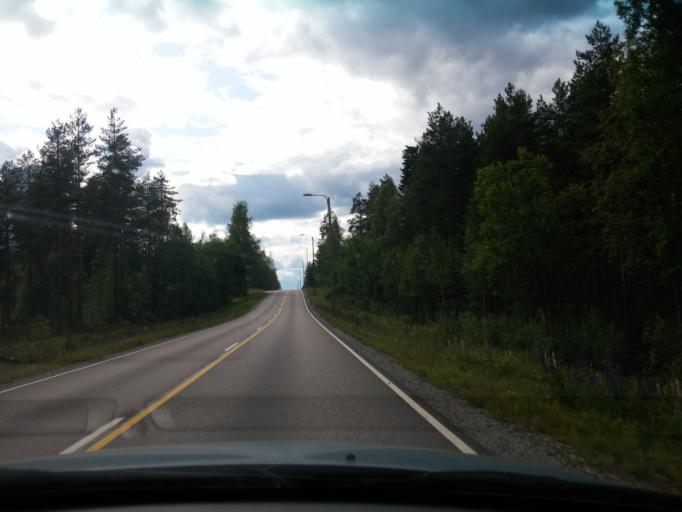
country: FI
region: Central Finland
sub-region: Saarijaervi-Viitasaari
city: Pylkoenmaeki
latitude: 62.6185
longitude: 24.7585
